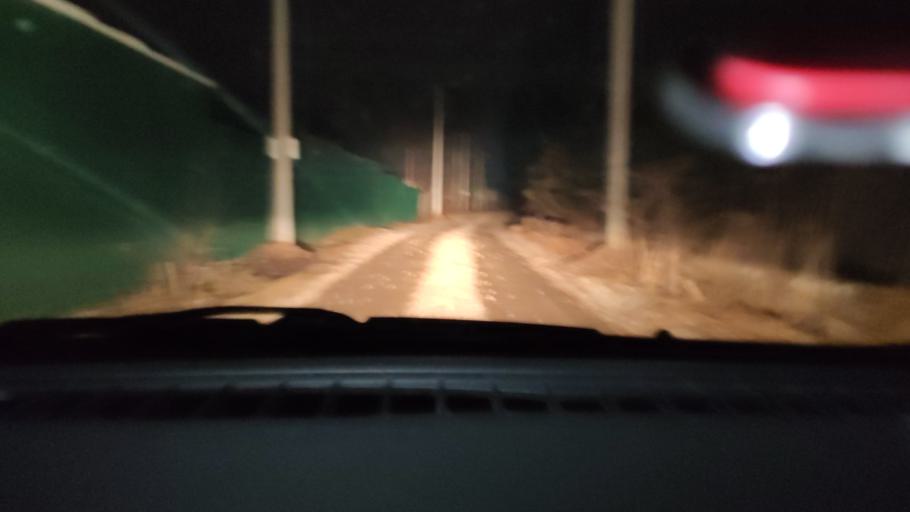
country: RU
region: Perm
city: Kondratovo
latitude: 58.0043
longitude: 56.0981
